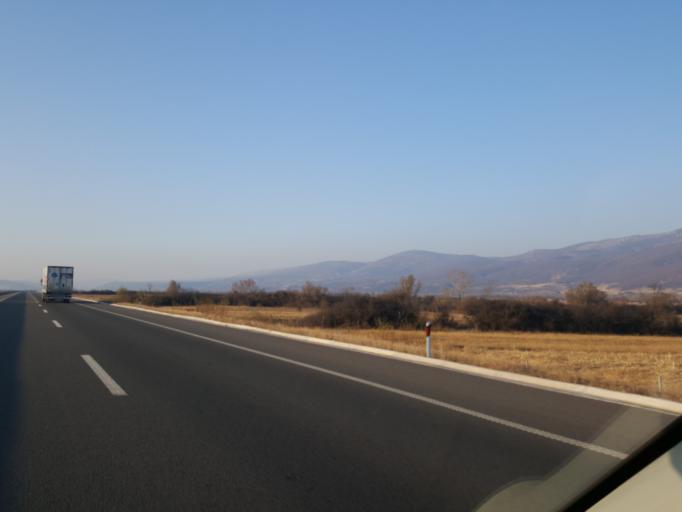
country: RS
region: Central Serbia
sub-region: Pirotski Okrug
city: Pirot
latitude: 43.0771
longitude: 22.6676
